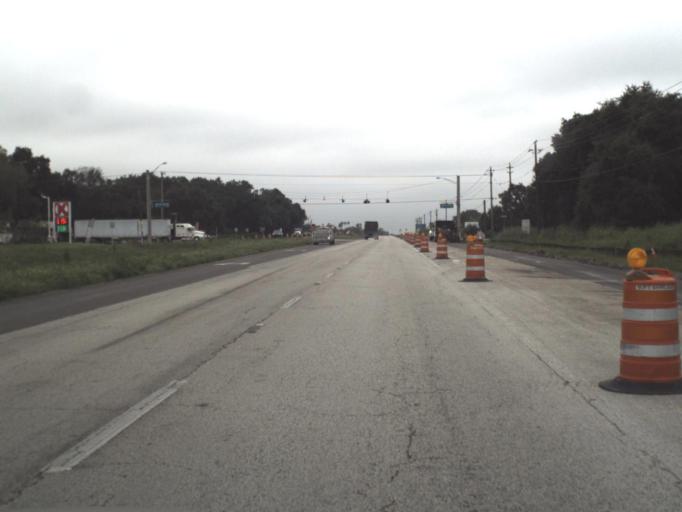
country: US
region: Florida
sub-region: Manatee County
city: Memphis
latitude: 27.6029
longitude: -82.5396
